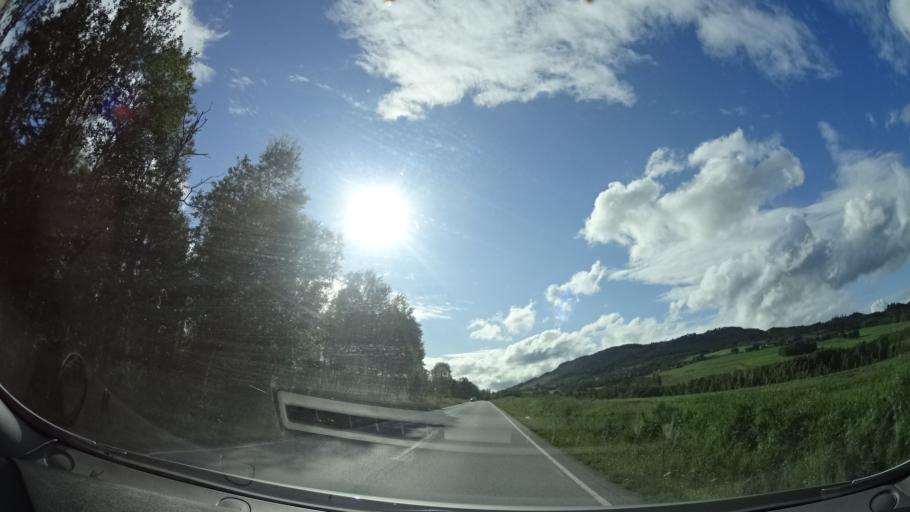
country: NO
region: More og Romsdal
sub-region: Halsa
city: Liaboen
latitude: 63.0719
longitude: 8.2762
